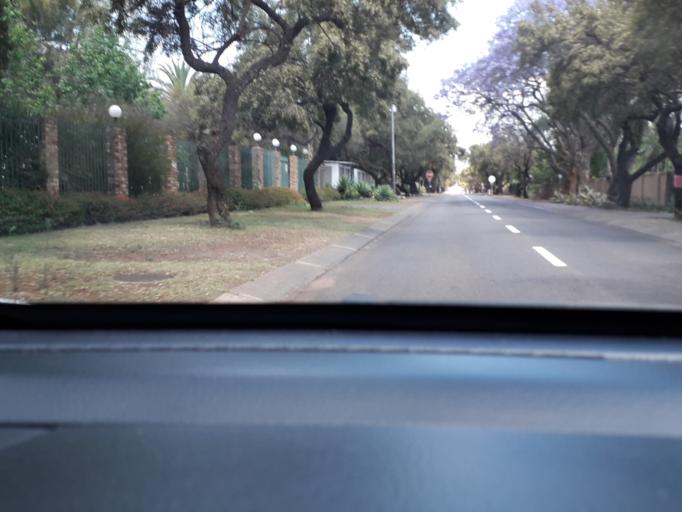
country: ZA
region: Gauteng
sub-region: City of Tshwane Metropolitan Municipality
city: Centurion
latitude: -25.8336
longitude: 28.2121
